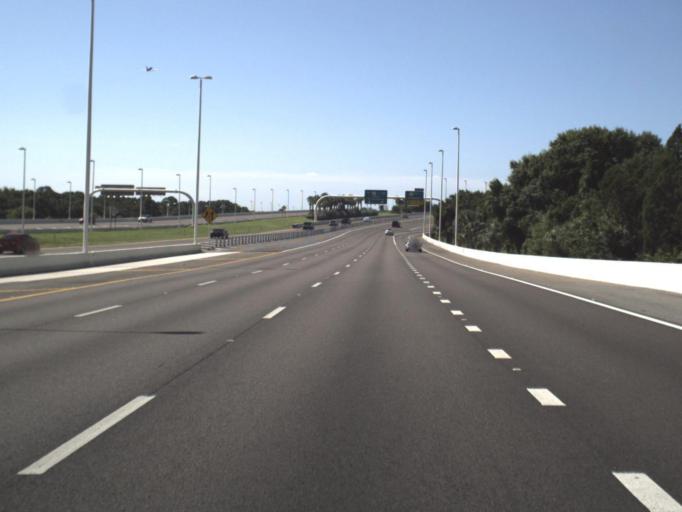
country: US
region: Florida
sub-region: Hillsborough County
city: Town 'n' Country
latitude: 27.9740
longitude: -82.5471
